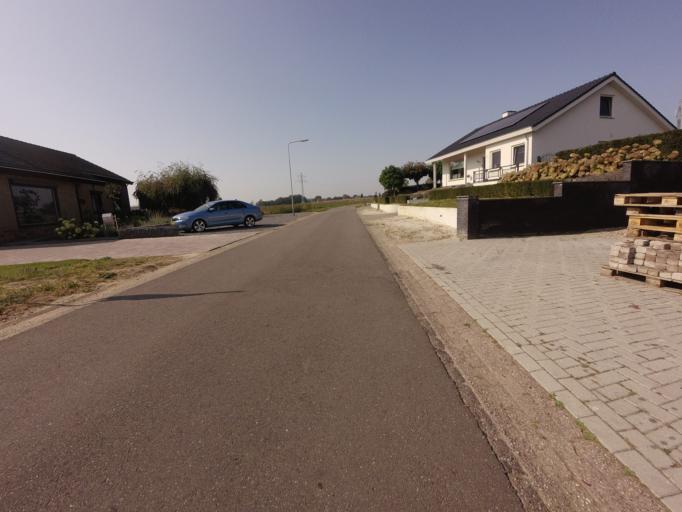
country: NL
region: Limburg
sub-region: Gemeente Beesel
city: Beesel
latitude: 51.2592
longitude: 5.9992
